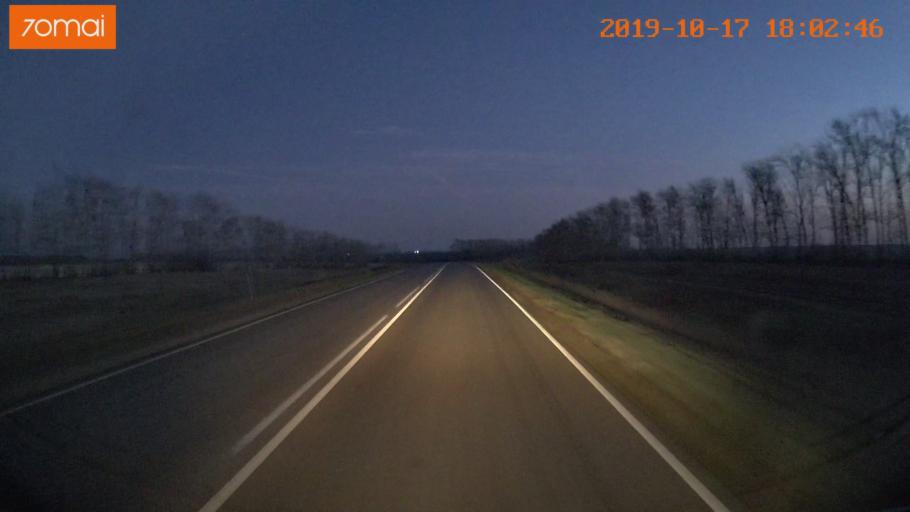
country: RU
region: Tula
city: Kurkino
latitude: 53.5030
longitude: 38.6177
